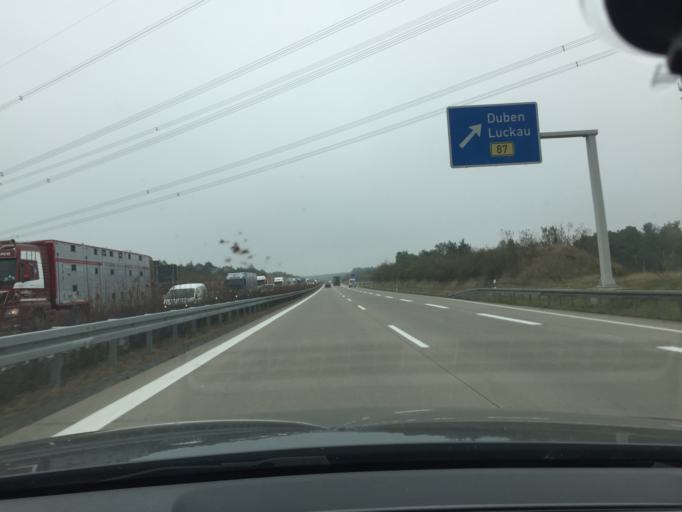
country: DE
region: Brandenburg
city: Luebben
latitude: 51.9029
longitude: 13.8083
